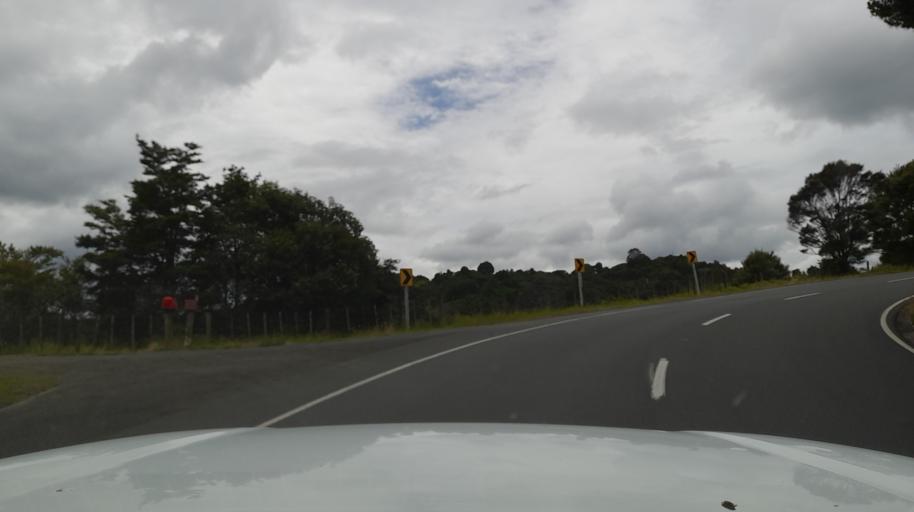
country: NZ
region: Northland
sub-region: Far North District
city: Kaitaia
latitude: -35.3568
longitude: 173.4873
